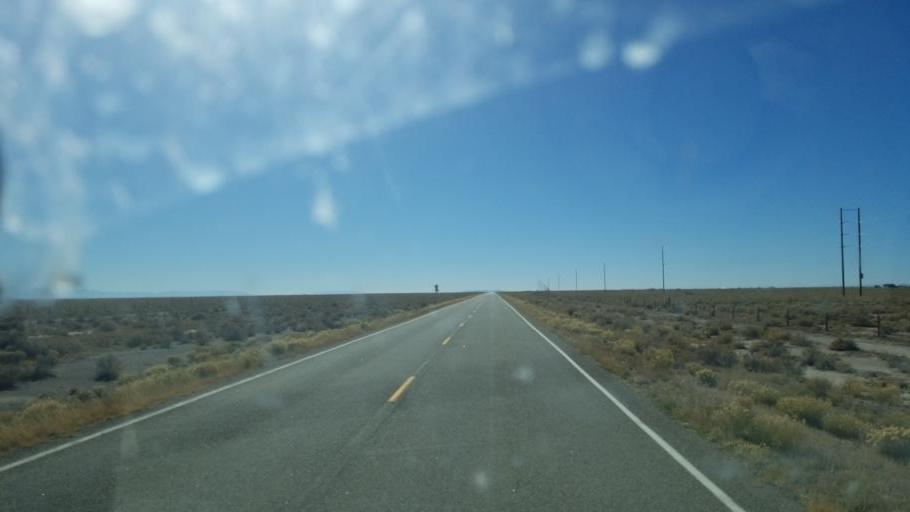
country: US
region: Colorado
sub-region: Saguache County
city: Center
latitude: 37.8546
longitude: -105.8924
